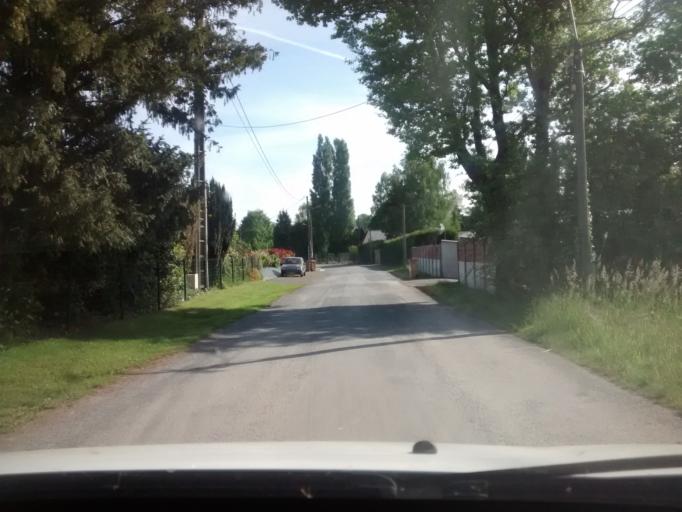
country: FR
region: Brittany
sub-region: Departement d'Ille-et-Vilaine
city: Fougeres
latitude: 48.3418
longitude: -1.2141
